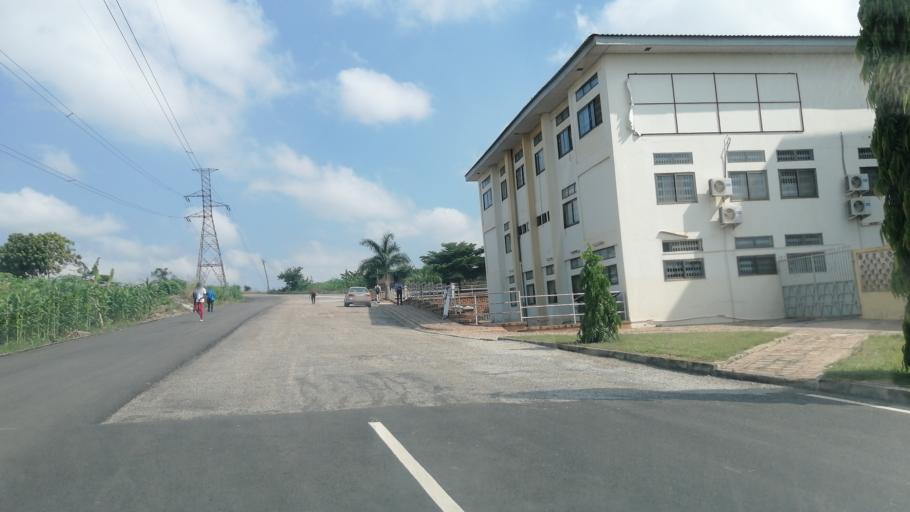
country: GH
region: Ashanti
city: Kumasi
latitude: 6.7003
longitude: -1.6774
